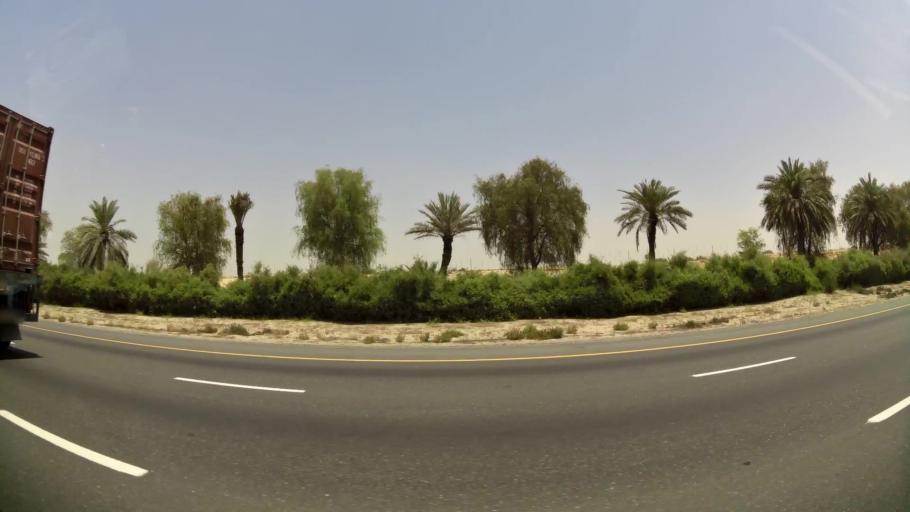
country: AE
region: Dubai
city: Dubai
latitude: 25.0589
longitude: 55.2732
